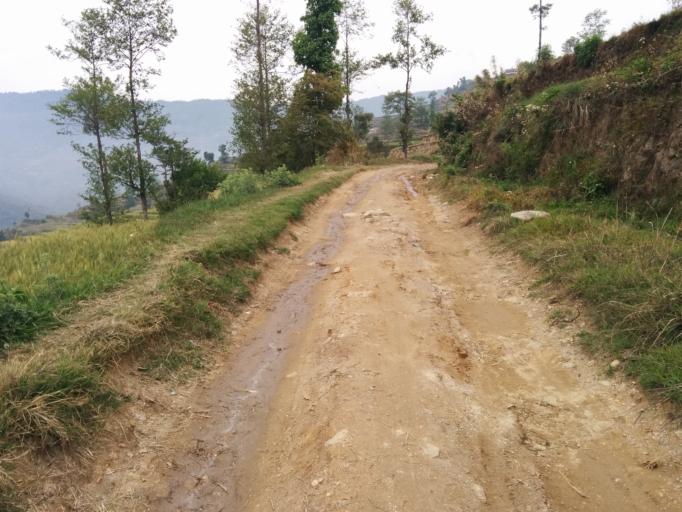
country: NP
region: Central Region
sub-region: Bagmati Zone
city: Bhaktapur
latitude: 27.7751
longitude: 85.4295
